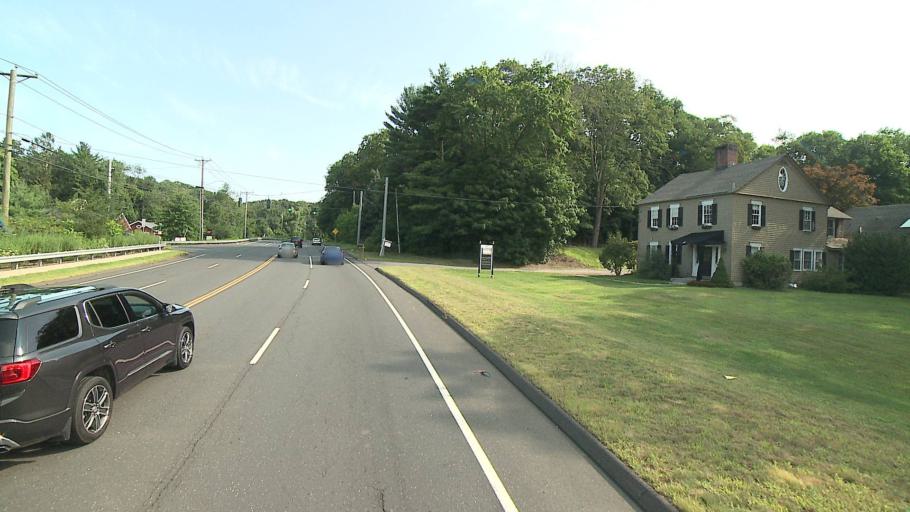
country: US
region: Connecticut
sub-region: Fairfield County
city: Wilton
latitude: 41.2176
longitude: -73.4283
